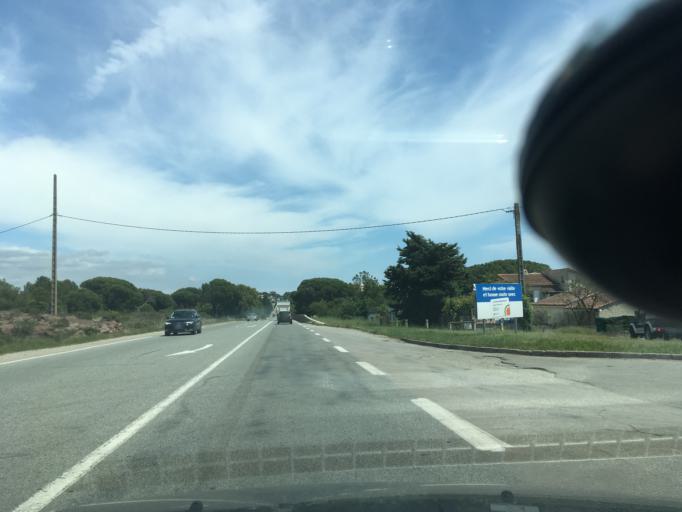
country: FR
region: Provence-Alpes-Cote d'Azur
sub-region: Departement du Var
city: Puget-sur-Argens
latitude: 43.4587
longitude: 6.6715
